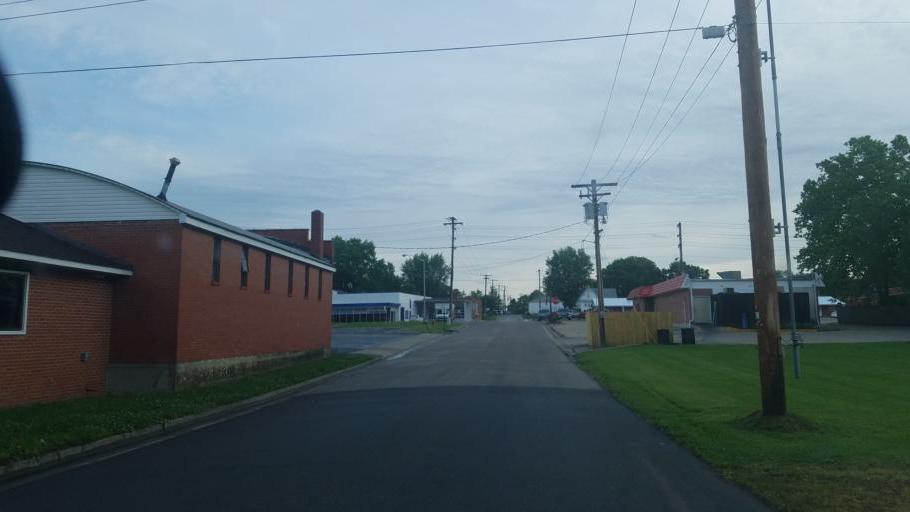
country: US
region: Missouri
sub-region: Moniteau County
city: California
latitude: 38.6268
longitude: -92.5726
